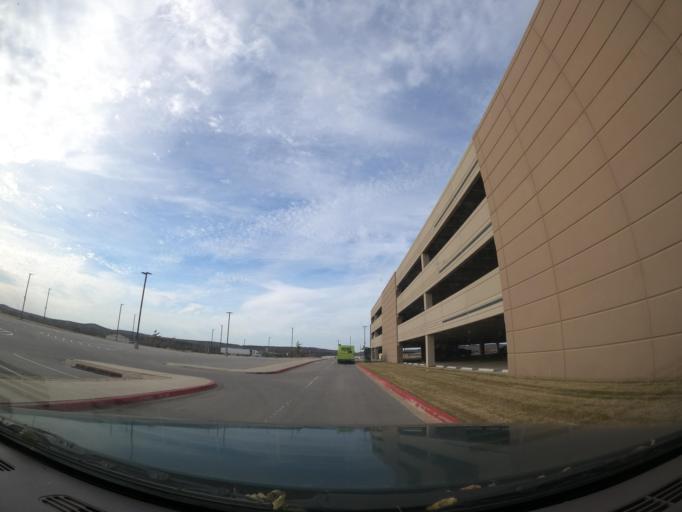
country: US
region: Oklahoma
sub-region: Tulsa County
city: Turley
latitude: 36.2070
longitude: -96.0052
